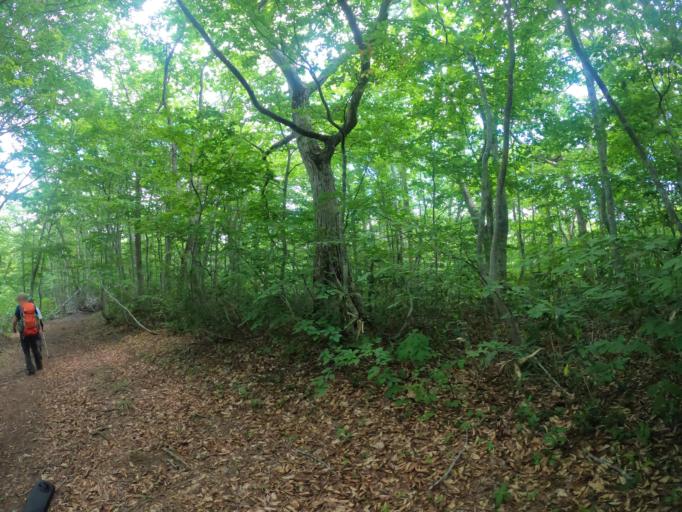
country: JP
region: Iwate
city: Ichinoseki
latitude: 38.9223
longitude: 140.7981
